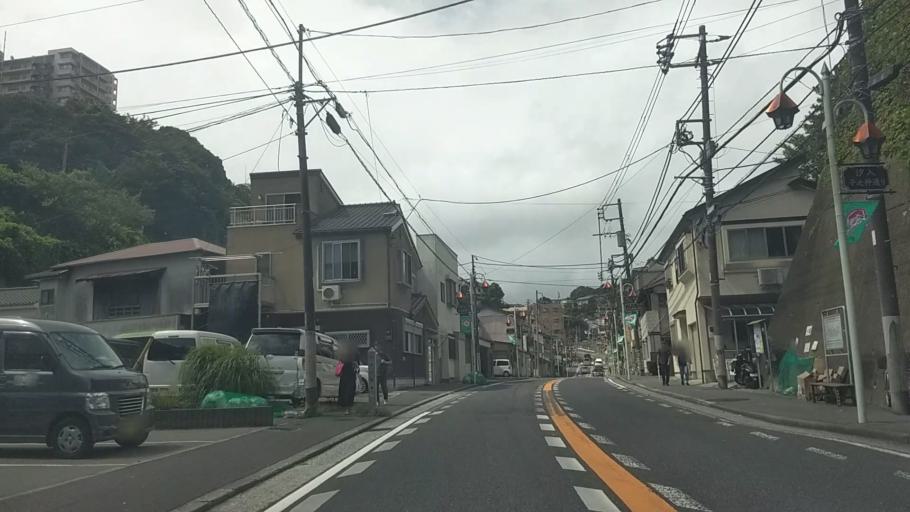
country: JP
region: Kanagawa
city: Yokosuka
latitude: 35.2765
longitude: 139.6599
